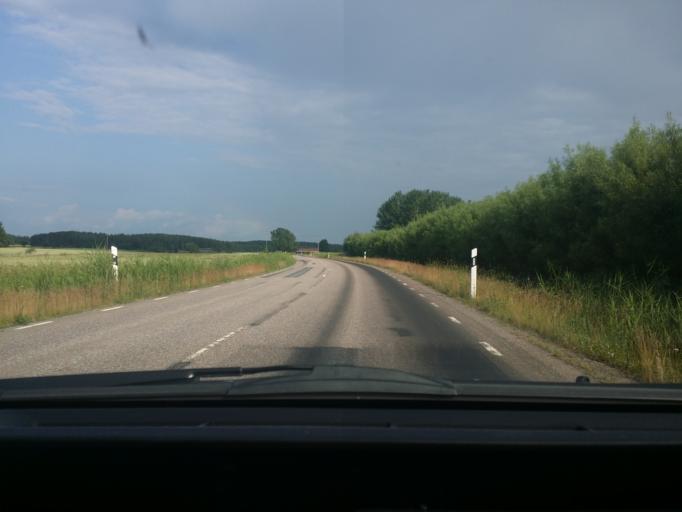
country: SE
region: Vaestmanland
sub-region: Hallstahammars Kommun
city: Kolback
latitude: 59.5588
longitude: 16.3292
